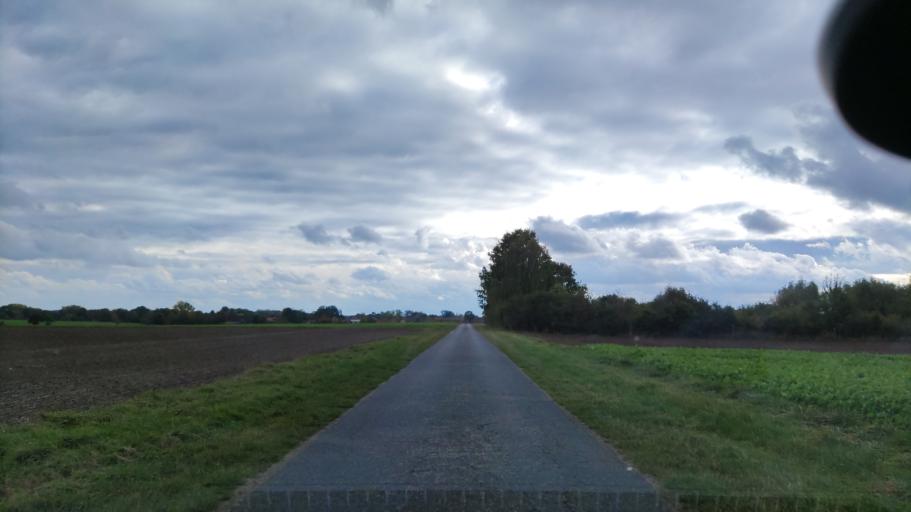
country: DE
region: Lower Saxony
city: Vastorf
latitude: 53.1539
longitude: 10.5350
